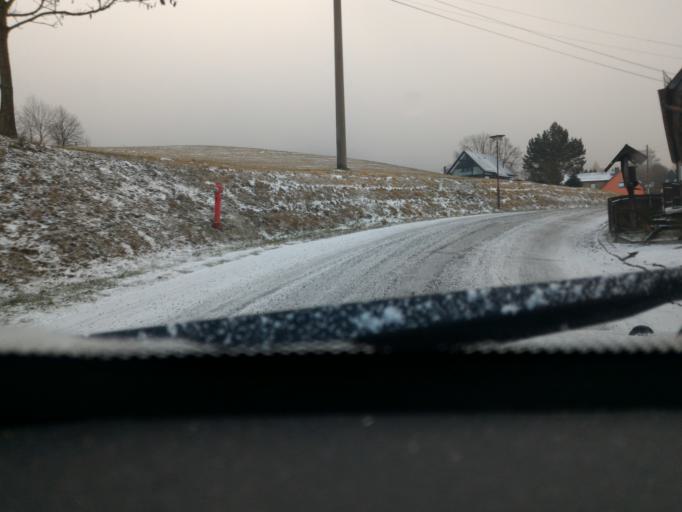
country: DE
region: Saxony
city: Grossschonau
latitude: 50.8609
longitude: 14.6526
